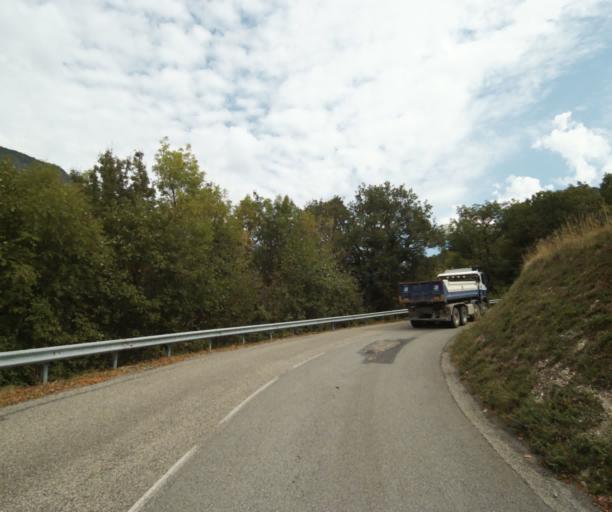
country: FR
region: Rhone-Alpes
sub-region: Departement de l'Isere
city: Saint-Egreve
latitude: 45.2539
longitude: 5.7002
